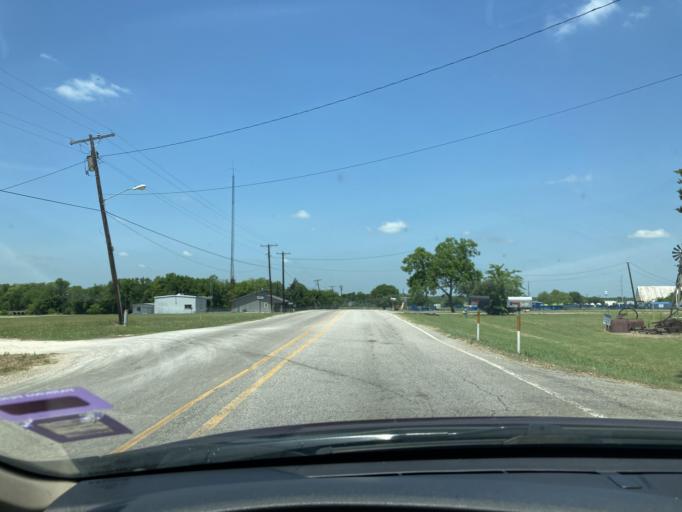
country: US
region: Texas
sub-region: Navarro County
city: Corsicana
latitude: 32.0658
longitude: -96.4611
